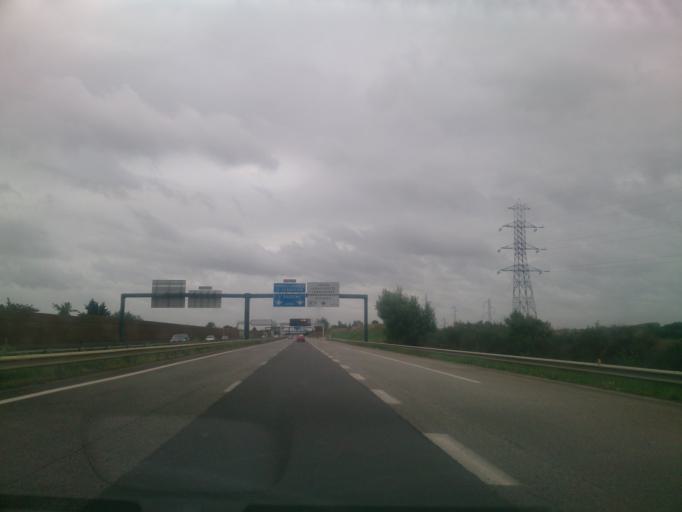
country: FR
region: Midi-Pyrenees
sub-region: Departement de la Haute-Garonne
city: Seysses
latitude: 43.4733
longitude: 1.3184
